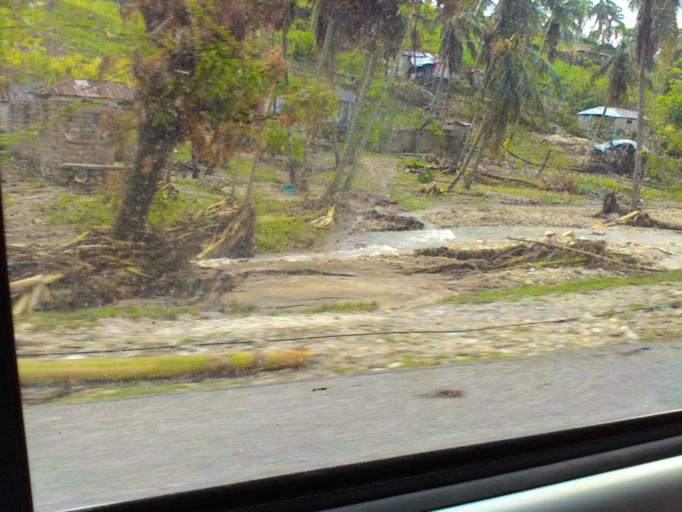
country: HT
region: Sud
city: Cavaillon
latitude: 18.2655
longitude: -73.7095
